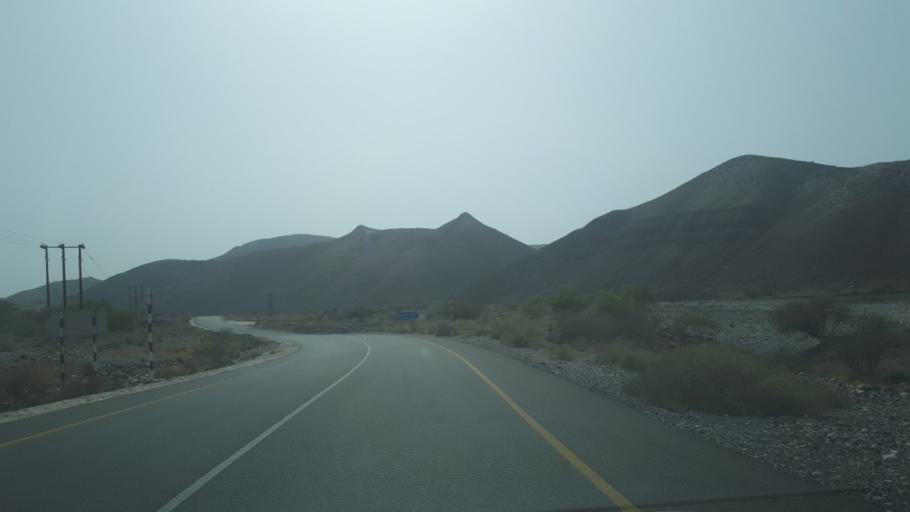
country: OM
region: Muhafazat ad Dakhiliyah
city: Bahla'
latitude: 23.2235
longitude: 56.9851
